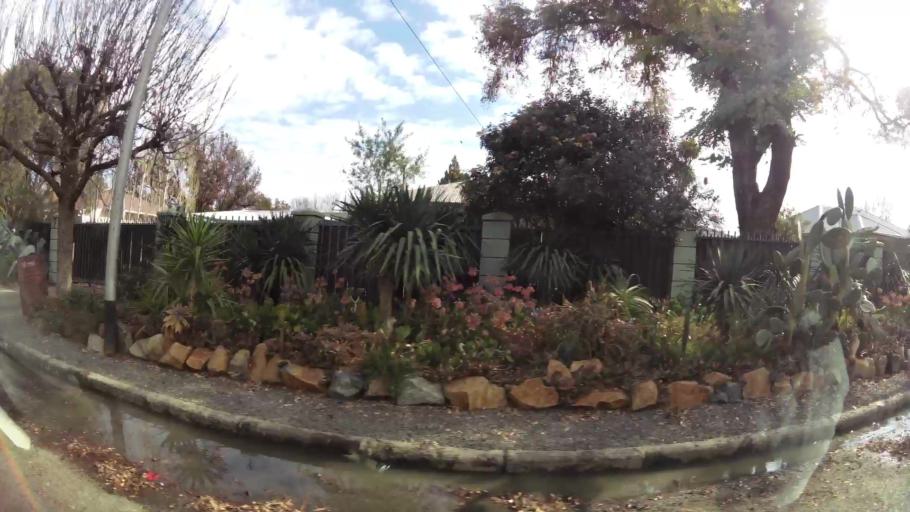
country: ZA
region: Orange Free State
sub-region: Mangaung Metropolitan Municipality
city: Bloemfontein
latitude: -29.0888
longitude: 26.2515
